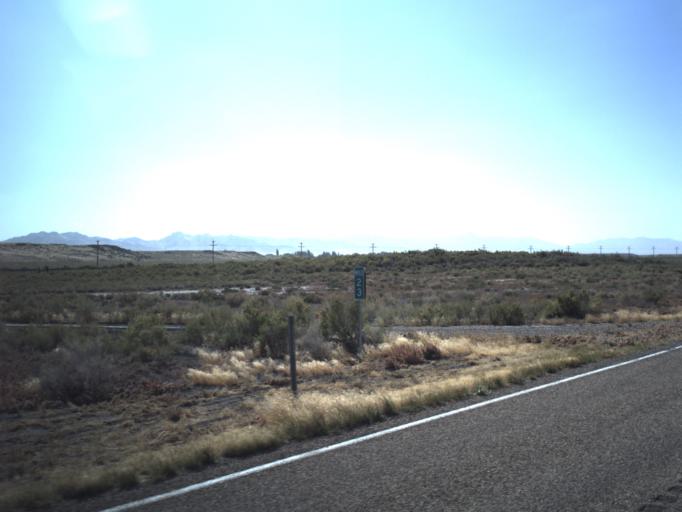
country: US
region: Utah
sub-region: Beaver County
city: Milford
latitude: 38.7266
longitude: -112.9672
